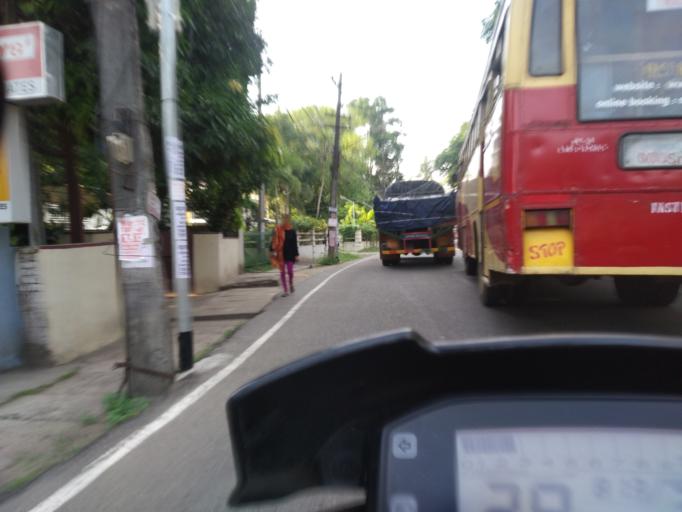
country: IN
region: Kerala
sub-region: Alappuzha
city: Arukutti
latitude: 9.9503
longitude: 76.3466
